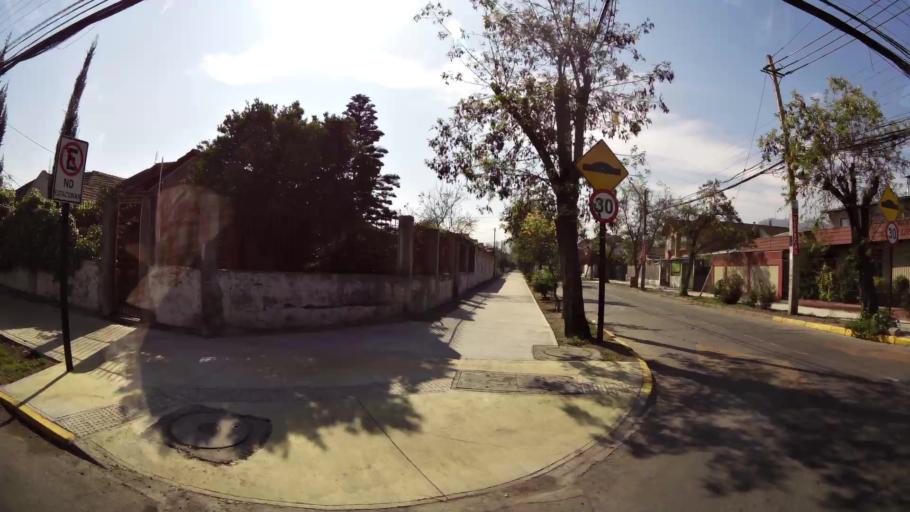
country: CL
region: Santiago Metropolitan
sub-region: Provincia de Santiago
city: Santiago
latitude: -33.4080
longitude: -70.6566
